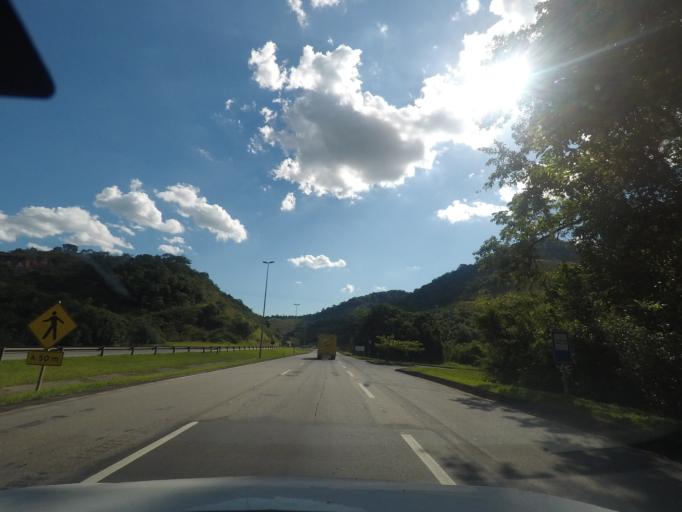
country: BR
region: Rio de Janeiro
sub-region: Guapimirim
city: Guapimirim
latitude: -22.5690
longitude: -43.0041
